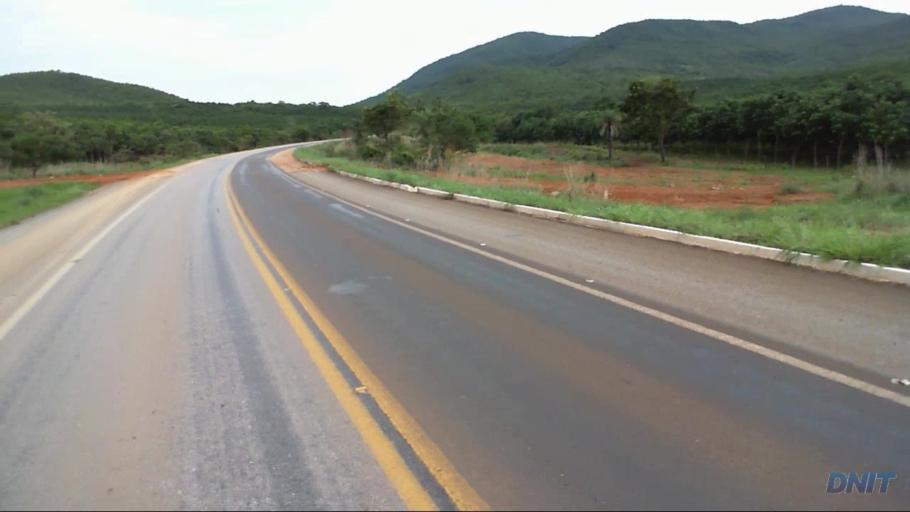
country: BR
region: Goias
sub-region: Barro Alto
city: Barro Alto
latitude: -14.9337
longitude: -48.9485
